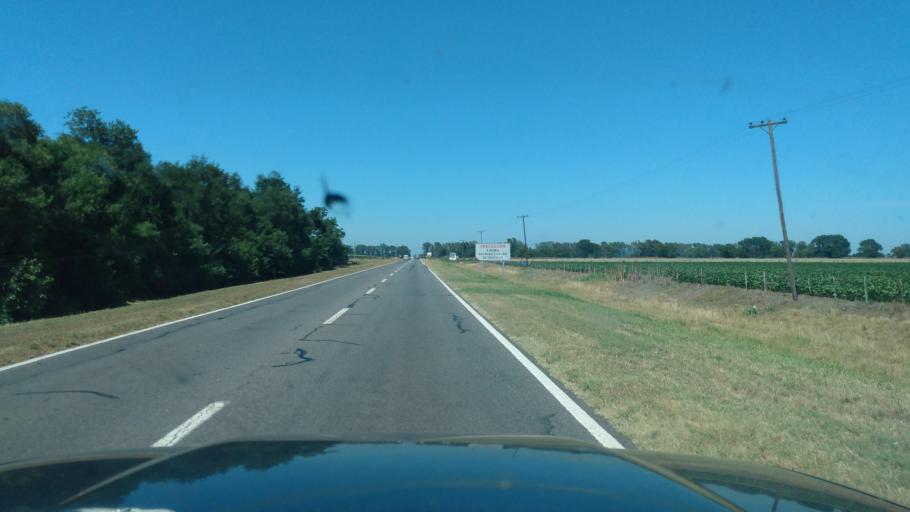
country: AR
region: Buenos Aires
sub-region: Partido de Bragado
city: Bragado
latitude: -35.0867
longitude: -60.3882
